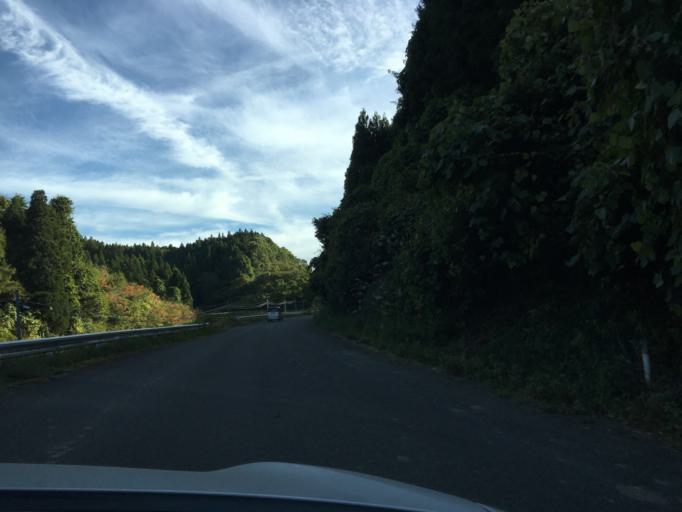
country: JP
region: Fukushima
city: Funehikimachi-funehiki
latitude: 37.2698
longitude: 140.6068
